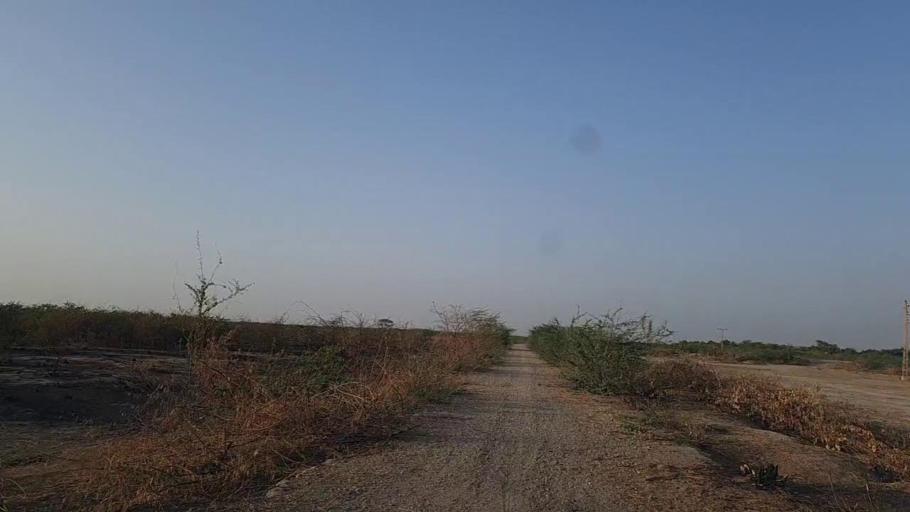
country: PK
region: Sindh
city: Naukot
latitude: 24.6448
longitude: 69.2520
